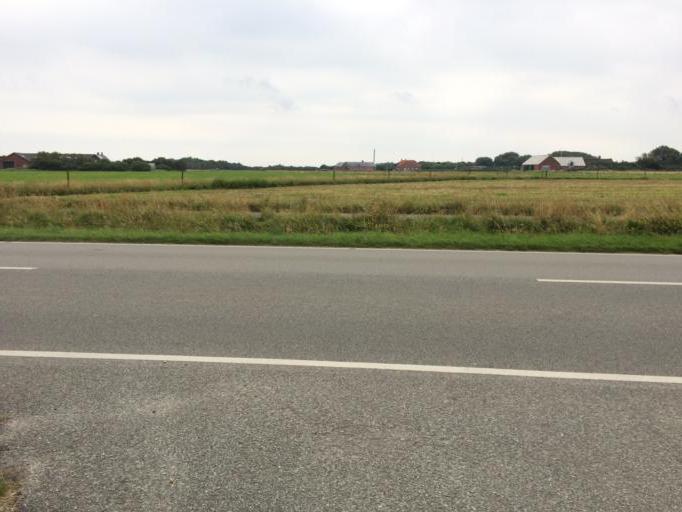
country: DK
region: South Denmark
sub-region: Fano Kommune
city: Nordby
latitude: 55.4276
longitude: 8.3913
